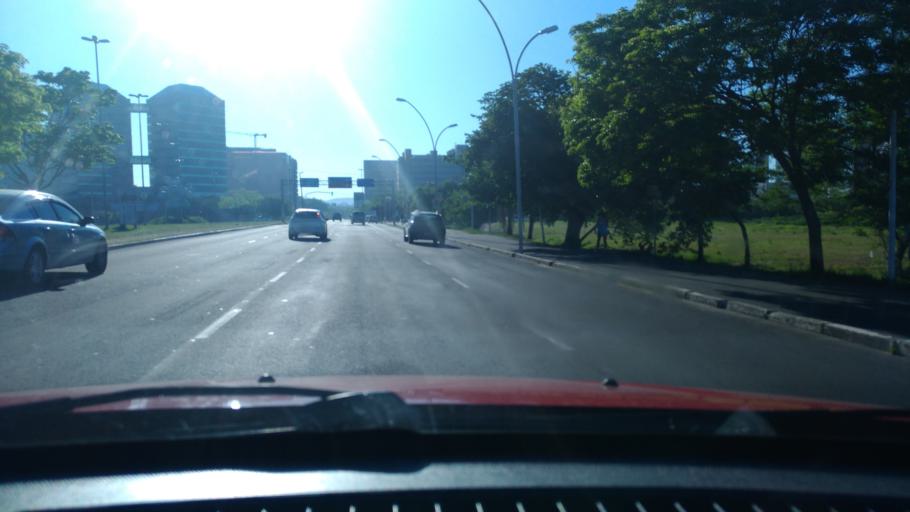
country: BR
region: Rio Grande do Sul
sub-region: Porto Alegre
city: Porto Alegre
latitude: -30.0426
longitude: -51.2353
